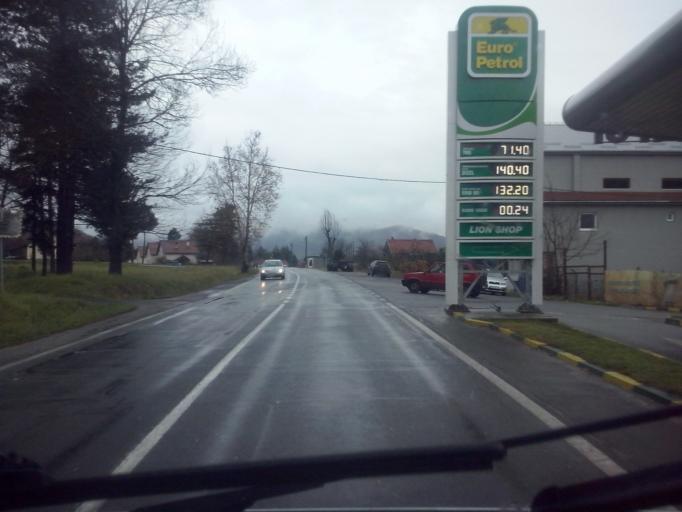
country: RS
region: Central Serbia
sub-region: Raski Okrug
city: Raska
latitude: 43.3914
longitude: 20.6352
